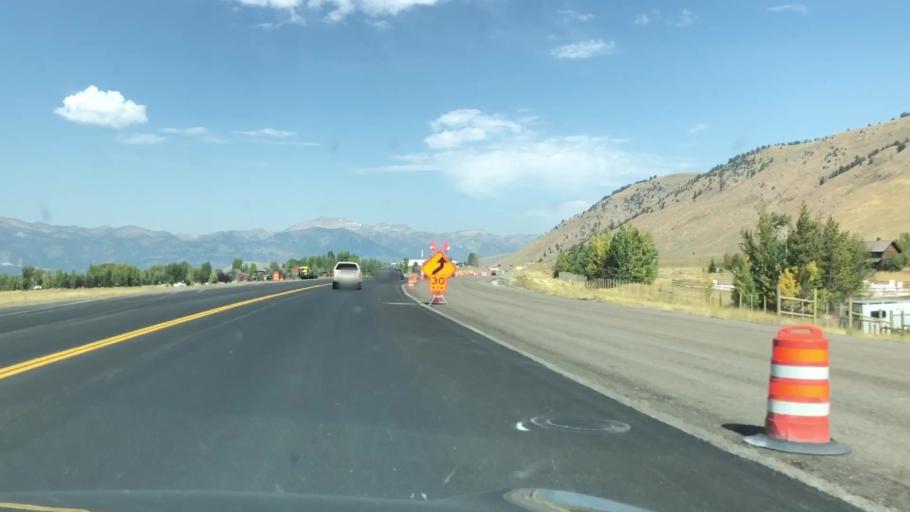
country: US
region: Wyoming
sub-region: Teton County
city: South Park
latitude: 43.4122
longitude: -110.7718
